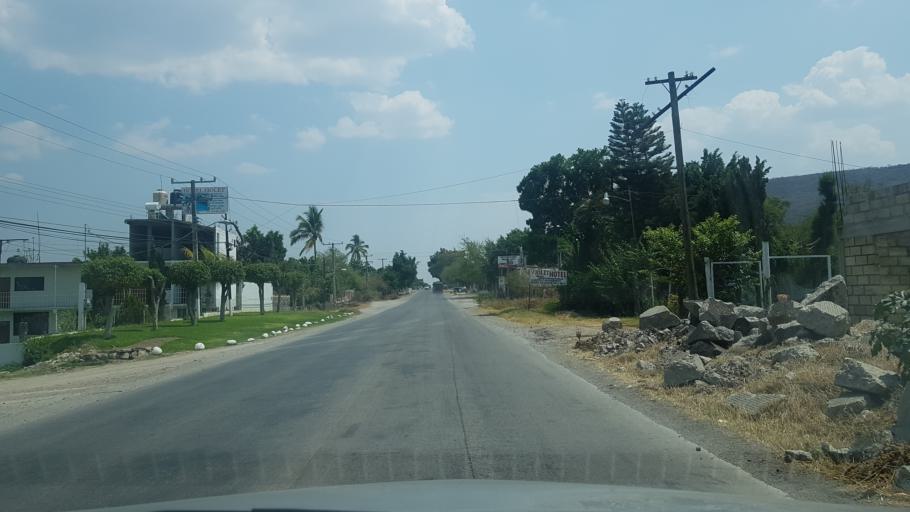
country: MX
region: Morelos
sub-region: Tlaltizapan de Zapata
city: Colonia Palo Prieto (Chipitongo)
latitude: 18.7244
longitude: -99.1225
